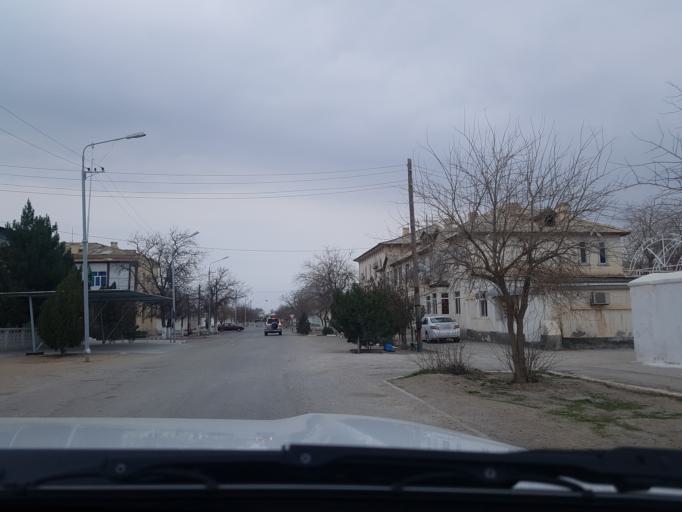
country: TM
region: Balkan
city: Balkanabat
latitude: 39.5014
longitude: 54.3702
